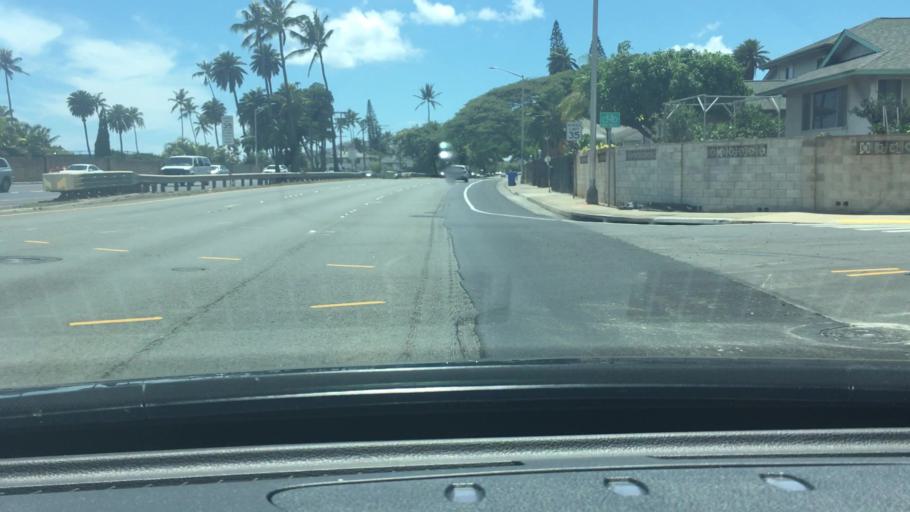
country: US
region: Hawaii
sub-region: Honolulu County
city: Waimanalo
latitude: 21.2771
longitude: -157.7587
